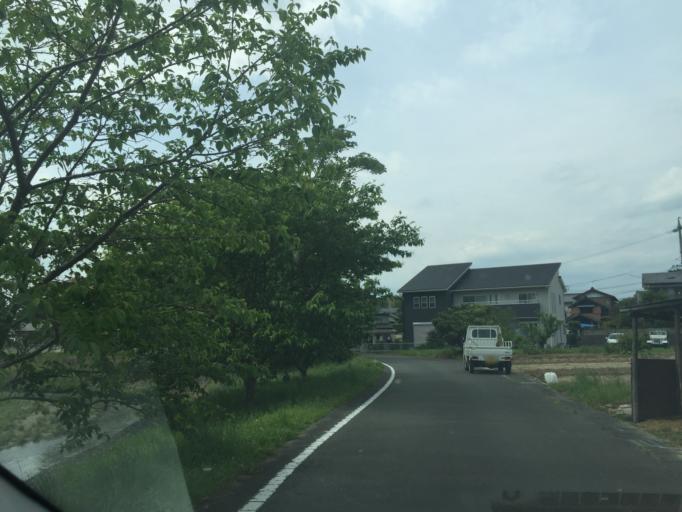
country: JP
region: Shizuoka
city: Kakegawa
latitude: 34.7778
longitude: 138.0389
